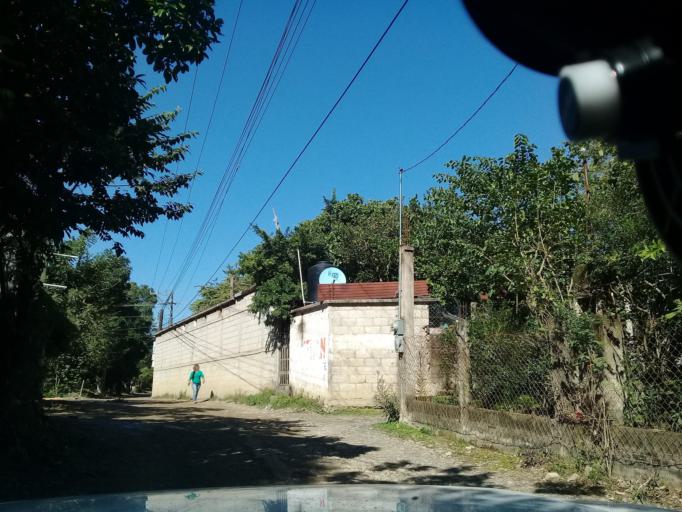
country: MX
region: Hidalgo
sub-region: Huejutla de Reyes
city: Huejutla de Reyes
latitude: 21.1609
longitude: -98.4125
